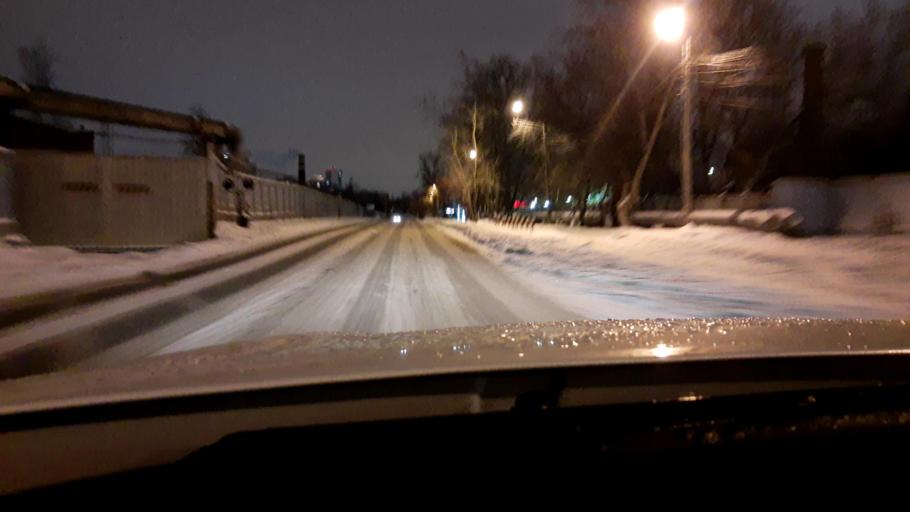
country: RU
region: Moscow
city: Khimki
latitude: 55.9032
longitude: 37.4386
